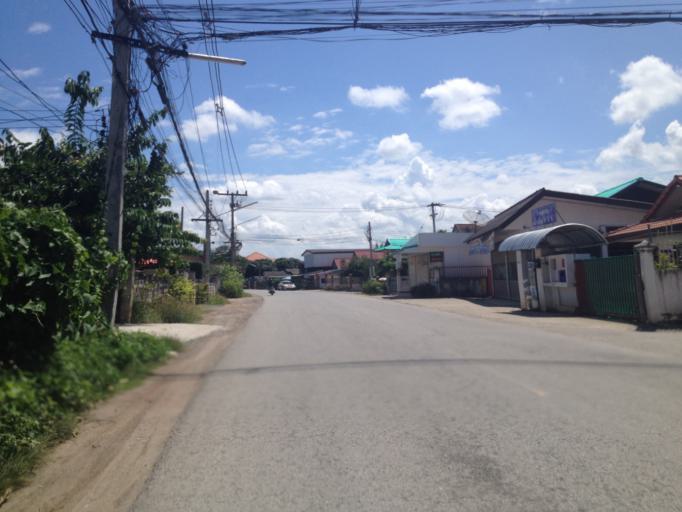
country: TH
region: Chiang Mai
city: Hang Dong
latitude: 18.6537
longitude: 98.9232
